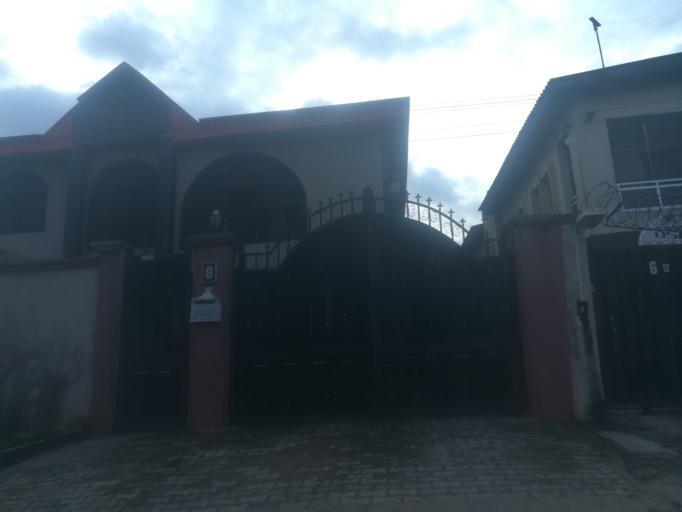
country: NG
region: Lagos
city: Somolu
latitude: 6.5457
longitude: 3.3824
